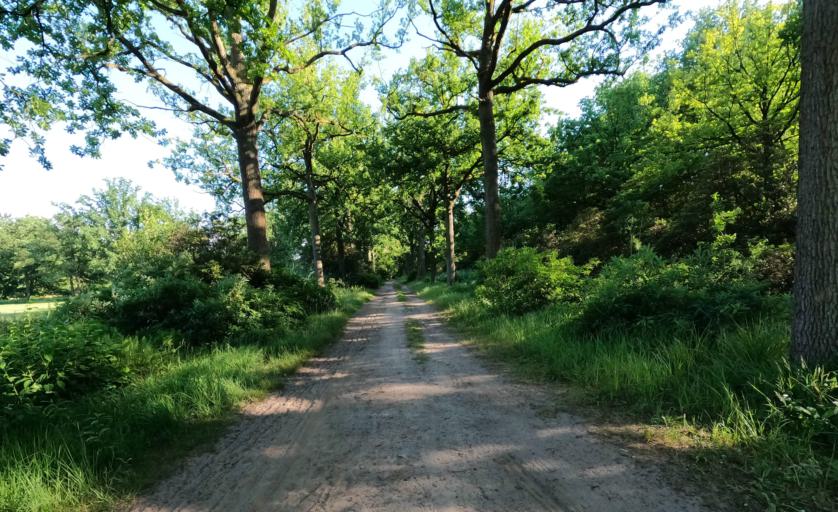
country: BE
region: Flanders
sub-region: Provincie Antwerpen
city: Schilde
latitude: 51.2585
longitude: 4.5706
